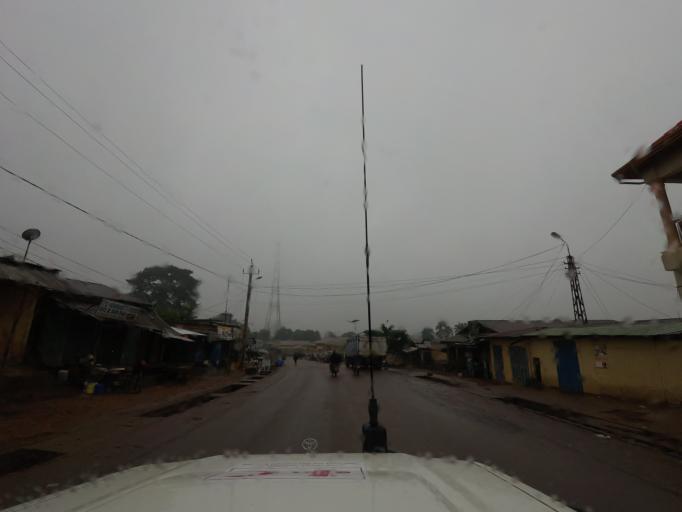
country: GN
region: Nzerekore
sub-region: Nzerekore Prefecture
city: Nzerekore
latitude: 7.7495
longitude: -8.8222
